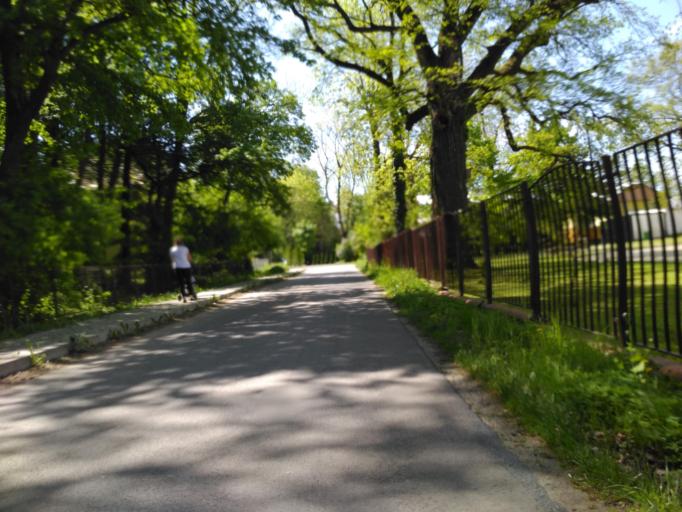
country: PL
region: Subcarpathian Voivodeship
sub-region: Powiat krosnienski
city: Miejsce Piastowe
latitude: 49.6015
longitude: 21.7978
